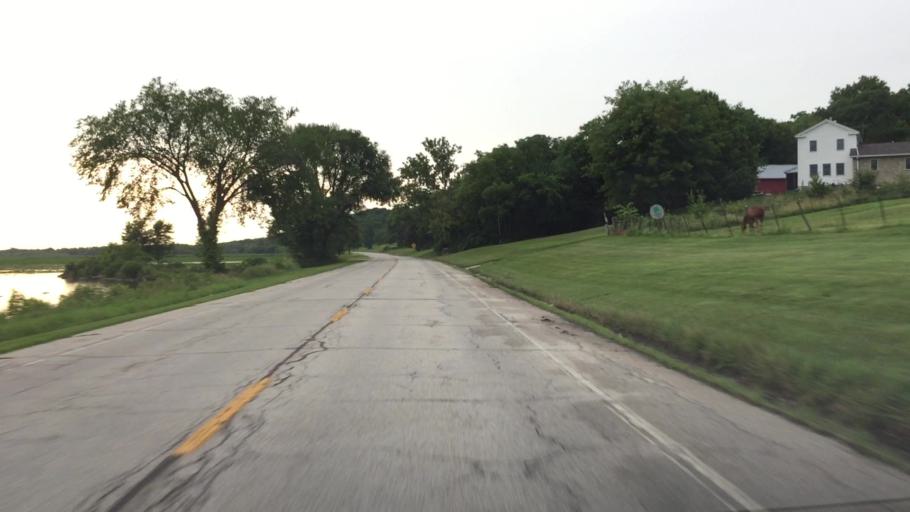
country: US
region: Illinois
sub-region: Hancock County
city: Nauvoo
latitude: 40.5234
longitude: -91.3665
